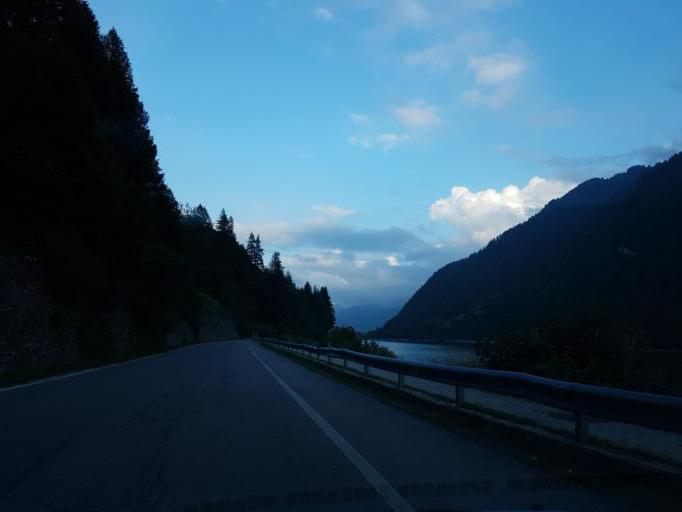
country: IT
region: Piedmont
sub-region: Provincia di Cuneo
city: Pontechianale
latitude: 44.6202
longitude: 7.0345
